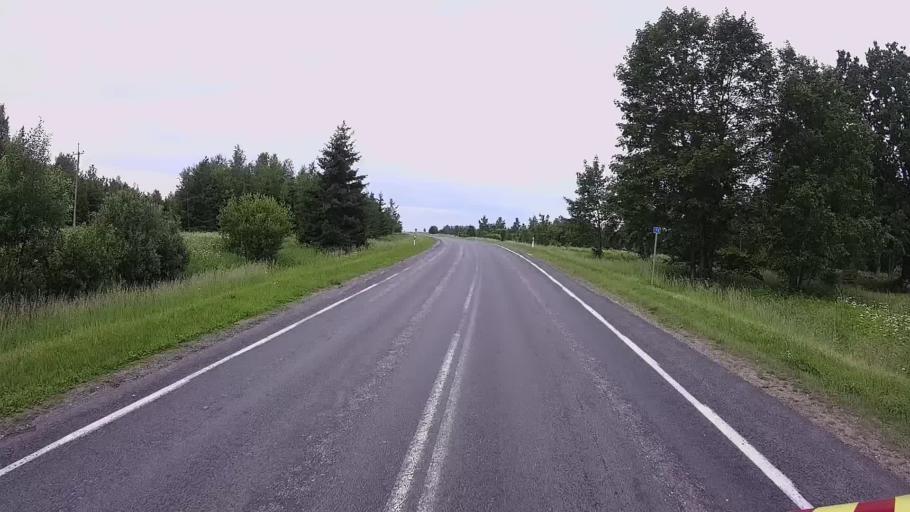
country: EE
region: Viljandimaa
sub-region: Karksi vald
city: Karksi-Nuia
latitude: 58.1841
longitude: 25.5953
